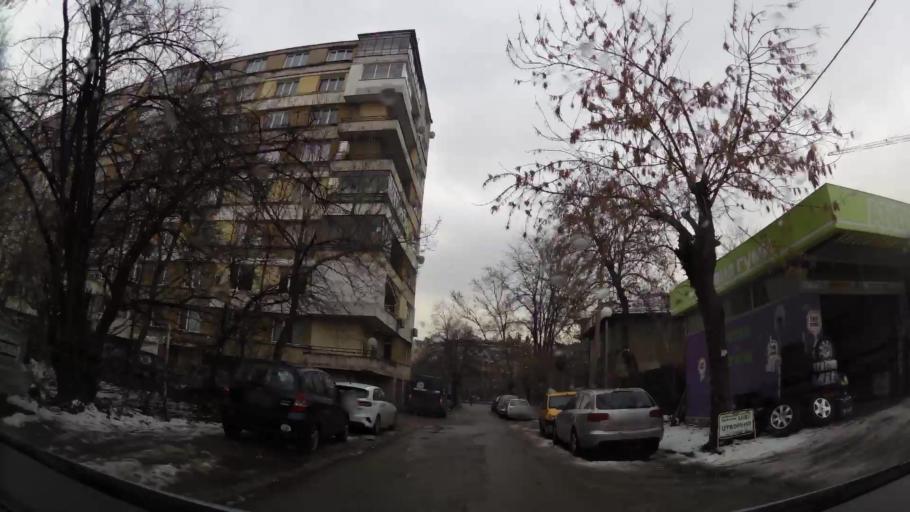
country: BG
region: Sofia-Capital
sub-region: Stolichna Obshtina
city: Sofia
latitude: 42.6791
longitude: 23.2934
